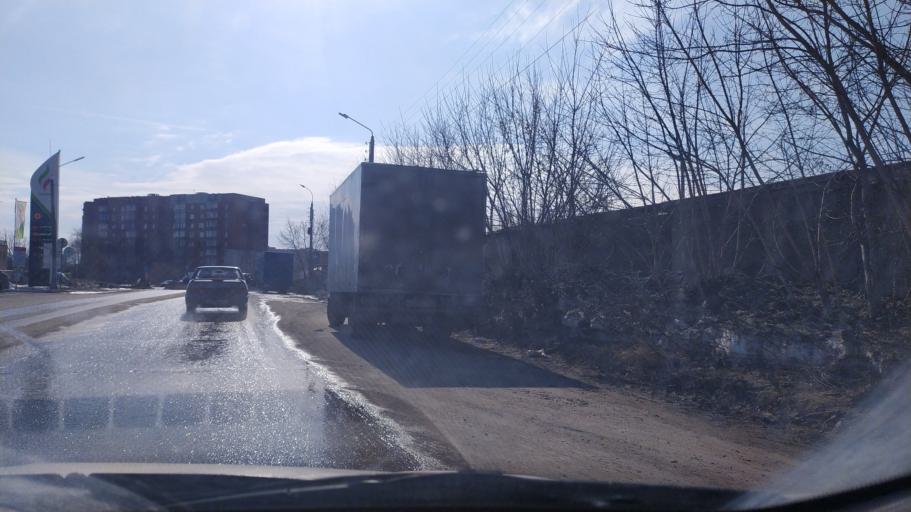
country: RU
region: Chuvashia
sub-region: Cheboksarskiy Rayon
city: Cheboksary
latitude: 56.1176
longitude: 47.2739
